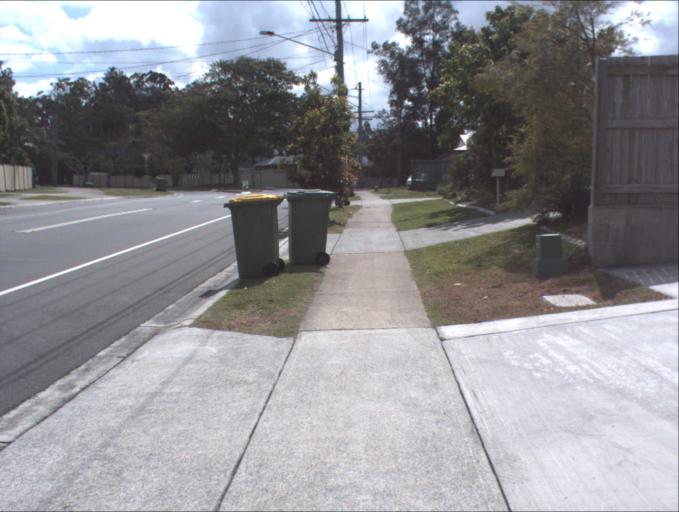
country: AU
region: Queensland
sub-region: Logan
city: Waterford West
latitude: -27.6836
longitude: 153.1334
